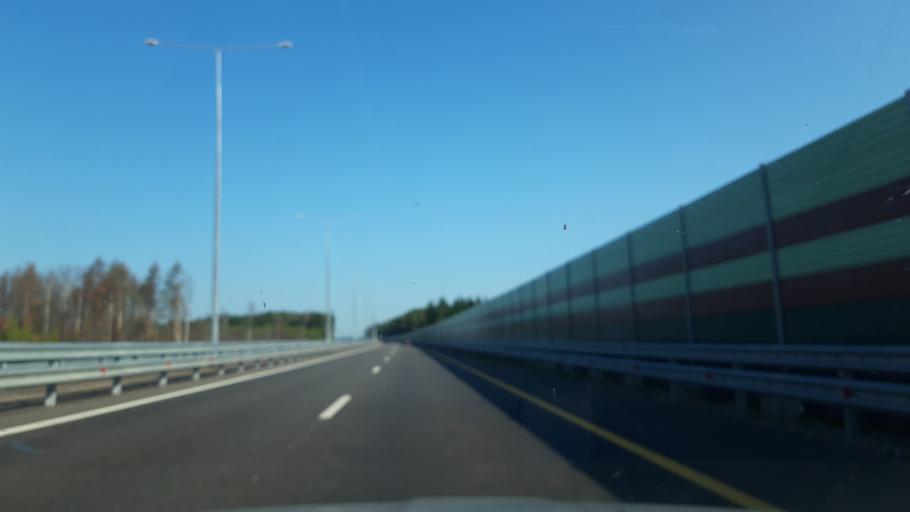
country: RU
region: Moskovskaya
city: Spas-Zaulok
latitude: 56.4804
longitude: 36.5382
